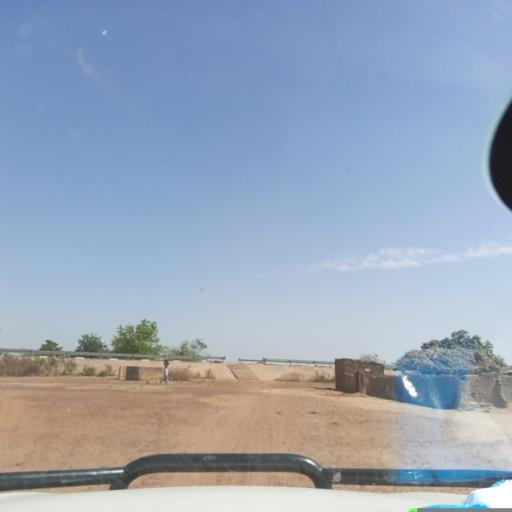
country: ML
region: Koulikoro
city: Dioila
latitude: 12.5210
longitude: -6.8080
